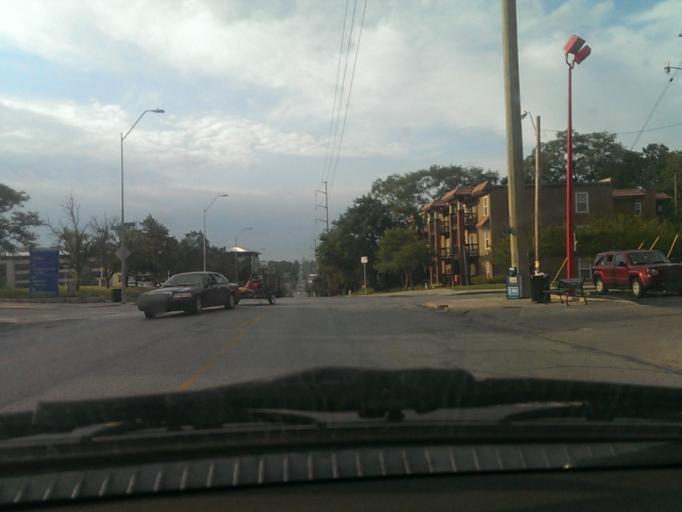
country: US
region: Kansas
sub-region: Johnson County
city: Westwood
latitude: 39.0339
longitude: -94.5733
